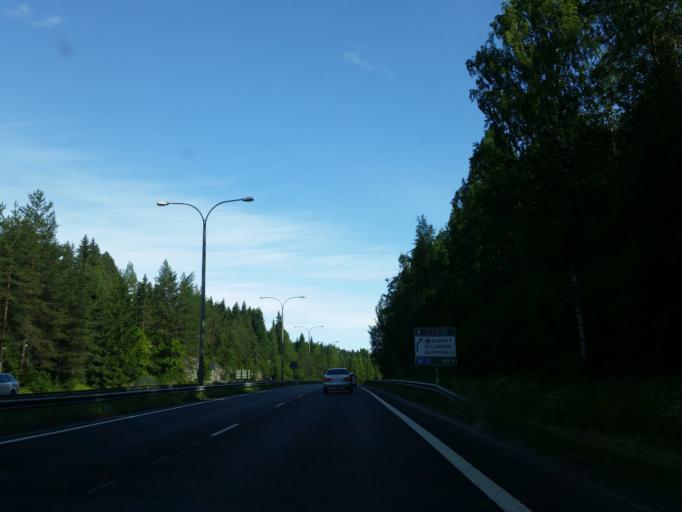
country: FI
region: Northern Savo
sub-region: Kuopio
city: Kuopio
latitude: 62.9143
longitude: 27.6819
